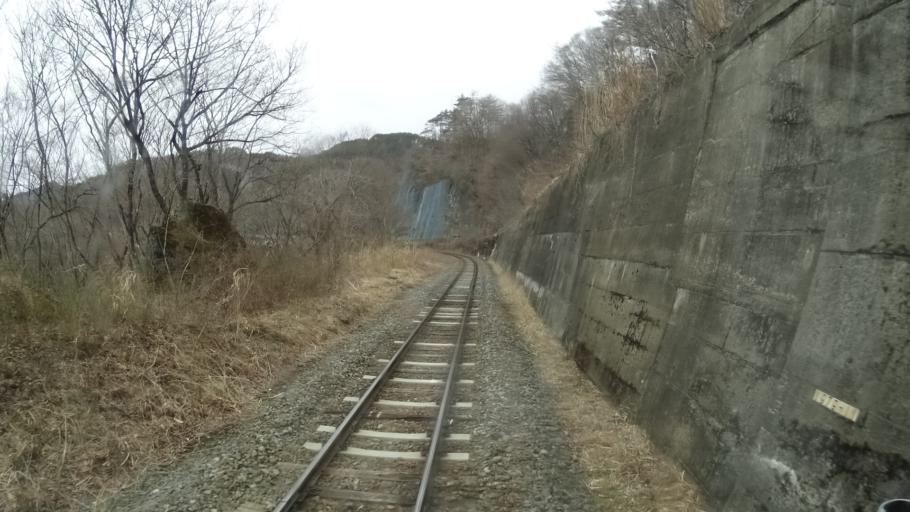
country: JP
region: Iwate
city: Tono
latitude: 39.3567
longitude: 141.3274
